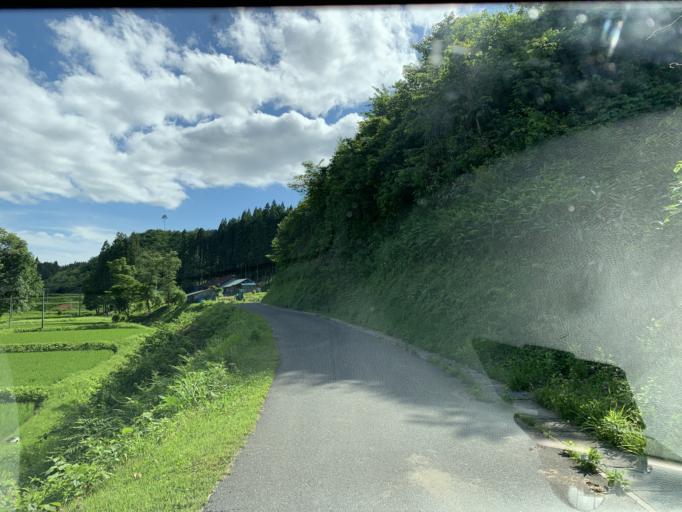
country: JP
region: Iwate
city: Ichinoseki
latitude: 38.9258
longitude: 140.9424
